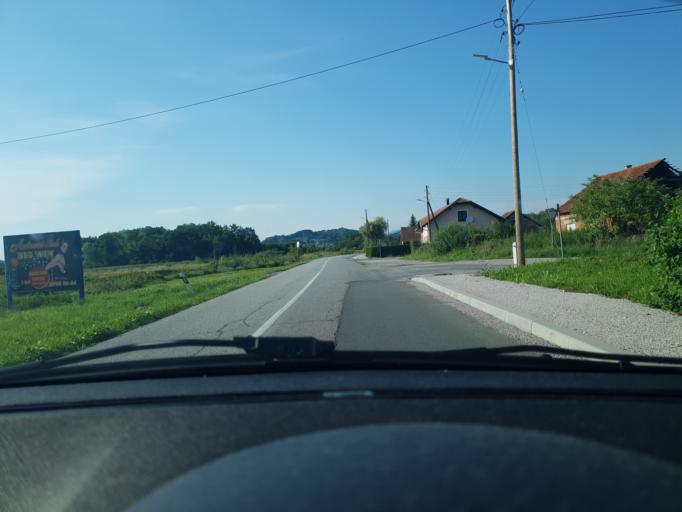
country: HR
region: Krapinsko-Zagorska
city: Oroslavje
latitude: 46.0046
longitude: 15.9306
